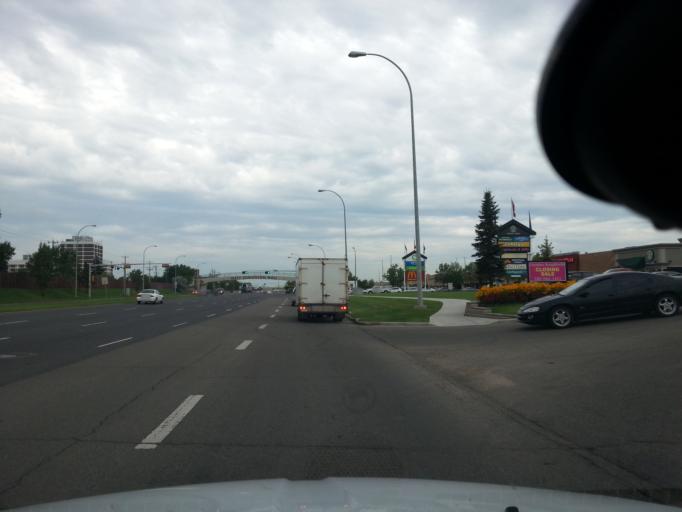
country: CA
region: Alberta
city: St. Albert
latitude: 53.5260
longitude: -113.6156
